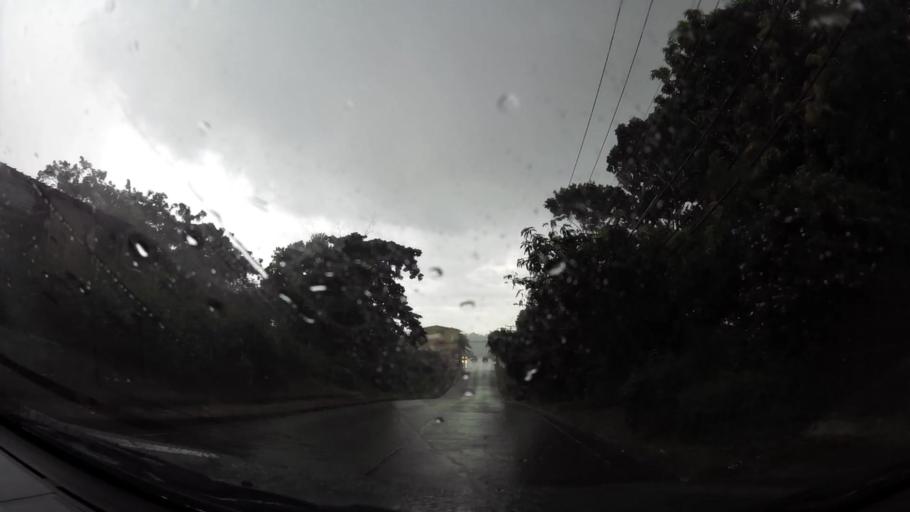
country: PA
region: Panama
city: San Miguelito
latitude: 9.0592
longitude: -79.4412
